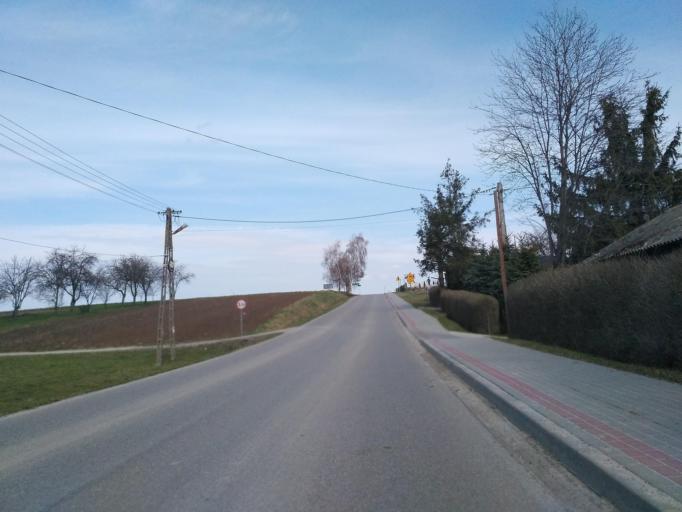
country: PL
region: Subcarpathian Voivodeship
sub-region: Powiat rzeszowski
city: Zglobien
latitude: 49.9932
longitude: 21.8023
